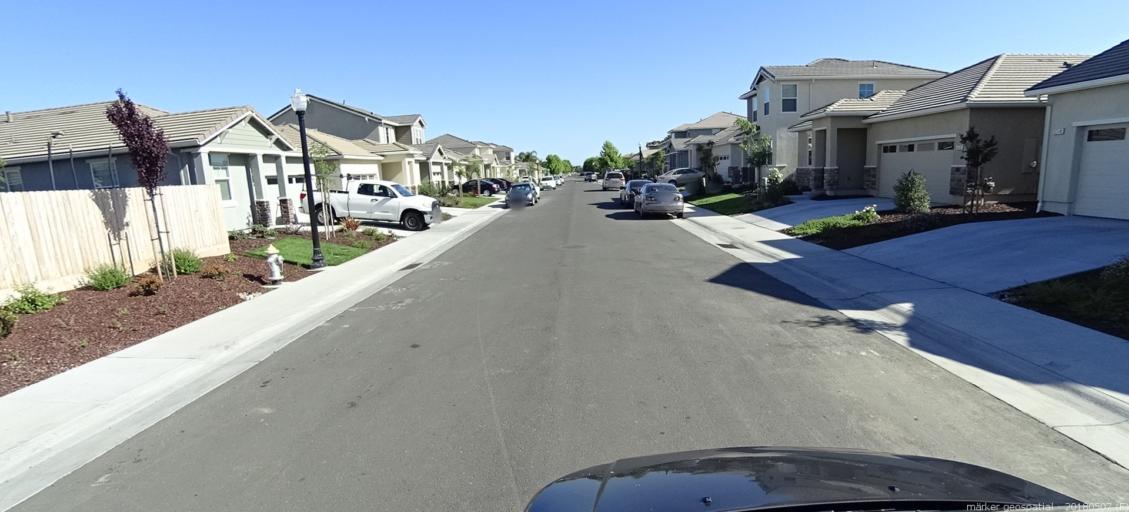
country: US
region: California
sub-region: Sacramento County
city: Rio Linda
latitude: 38.6756
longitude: -121.4939
